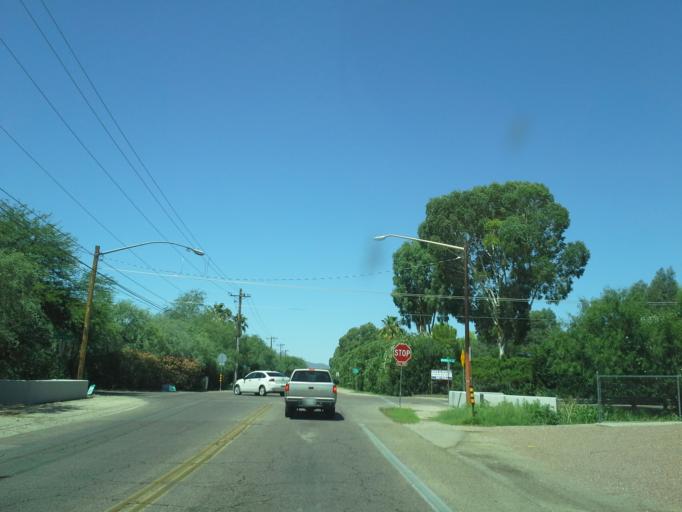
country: US
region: Arizona
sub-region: Pima County
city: Catalina Foothills
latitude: 32.2831
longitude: -110.9519
